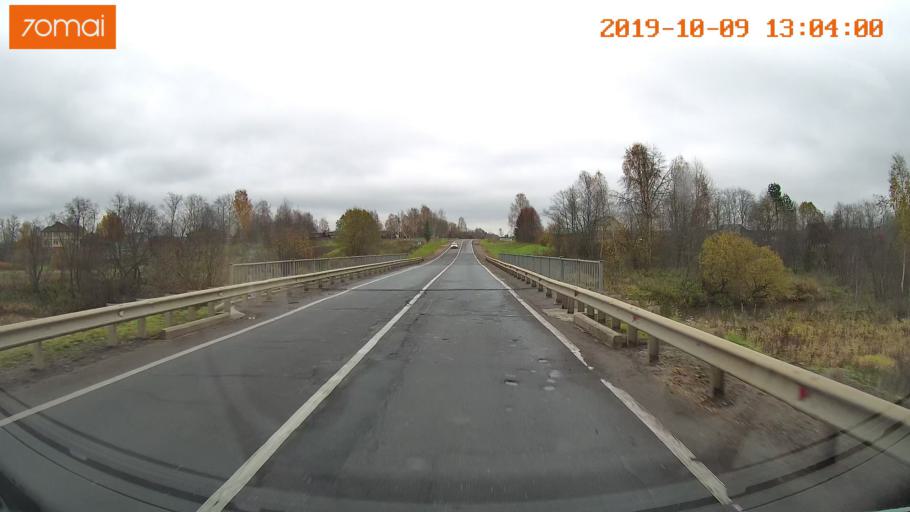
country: RU
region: Jaroslavl
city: Lyubim
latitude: 58.3584
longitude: 40.5434
